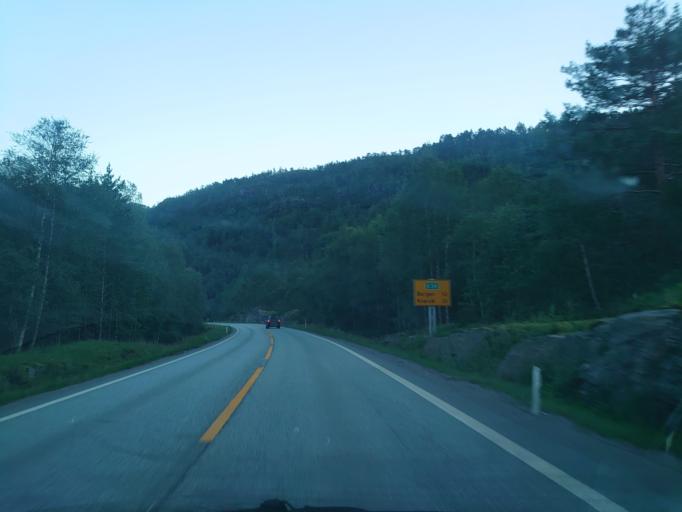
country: NO
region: Hordaland
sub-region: Osteroy
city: Lonevag
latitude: 60.6632
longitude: 5.4838
